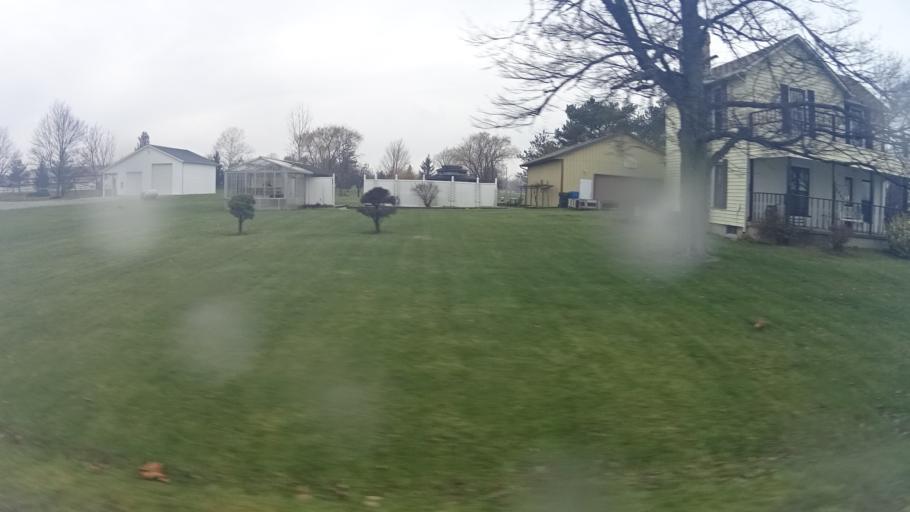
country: US
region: Ohio
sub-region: Lorain County
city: Lagrange
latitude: 41.2369
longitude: -82.1577
